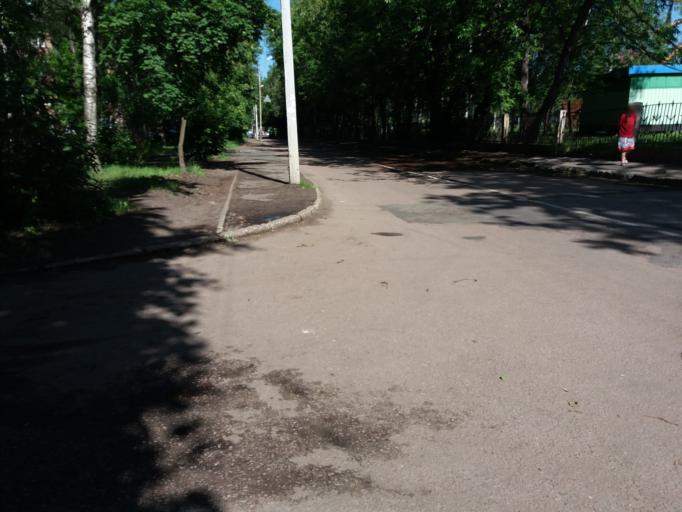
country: RU
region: Jaroslavl
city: Yaroslavl
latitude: 57.6357
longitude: 39.8535
